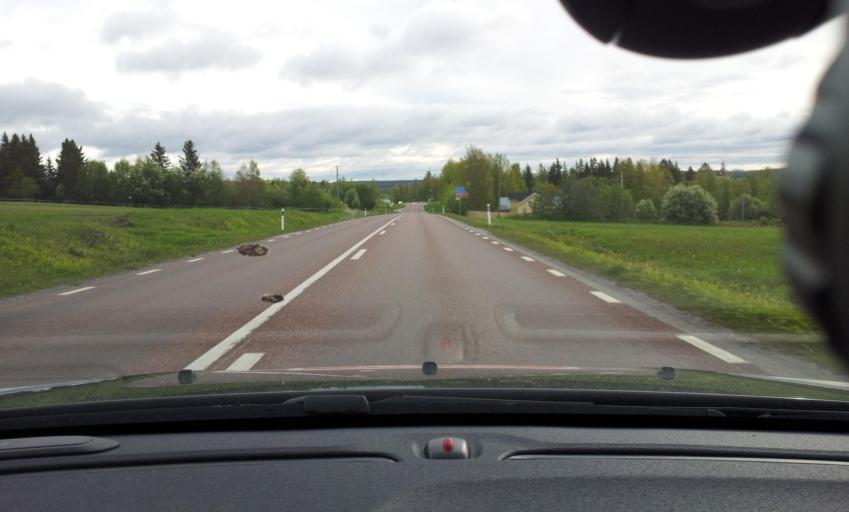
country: SE
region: Jaemtland
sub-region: OEstersunds Kommun
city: Brunflo
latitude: 63.0343
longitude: 14.8026
